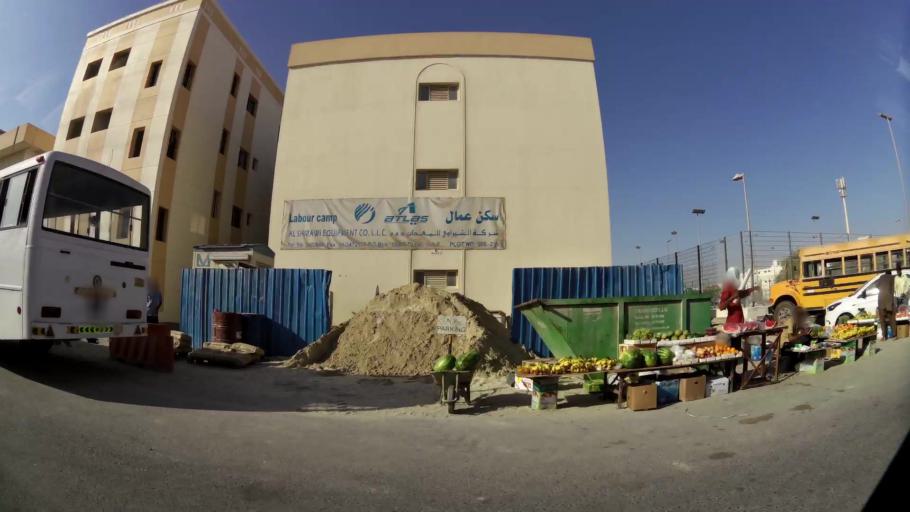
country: AE
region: Dubai
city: Dubai
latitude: 25.1233
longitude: 55.2296
